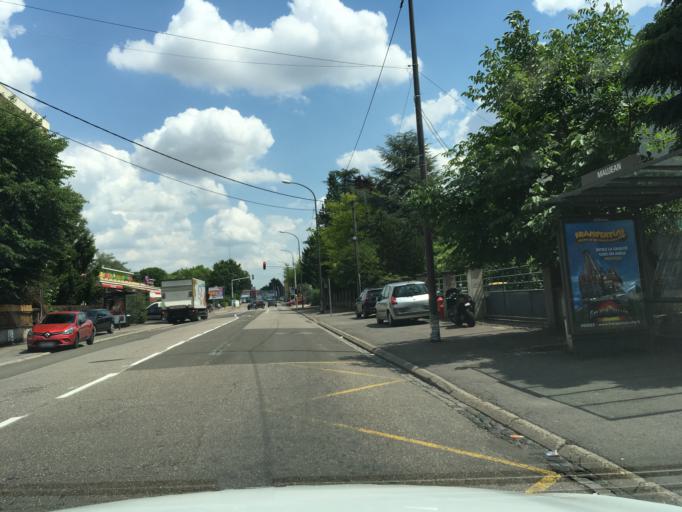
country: FR
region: Lorraine
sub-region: Departement de la Moselle
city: Saint-Julien-les-Metz
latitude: 49.1202
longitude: 6.2143
